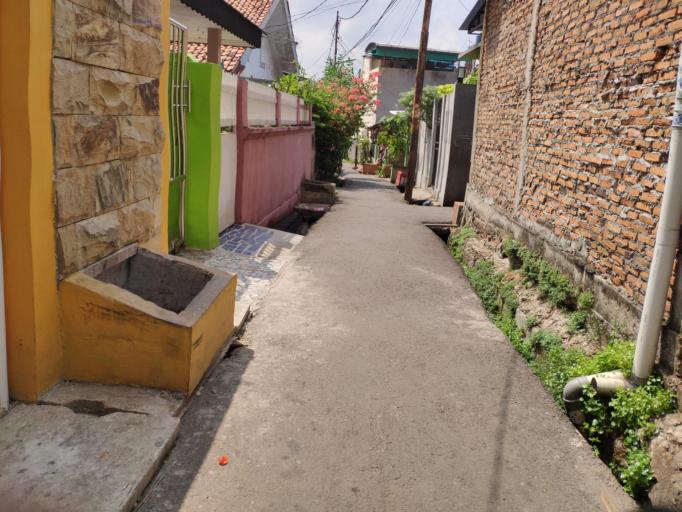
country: ID
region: Jakarta Raya
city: Jakarta
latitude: -6.2037
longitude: 106.8718
